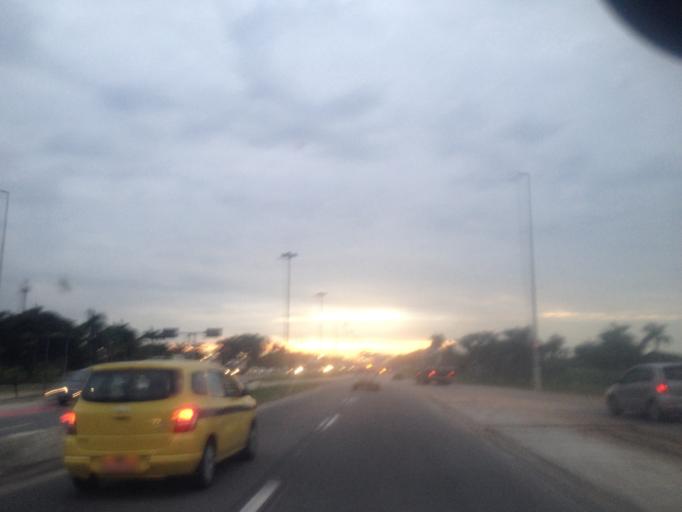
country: BR
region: Rio de Janeiro
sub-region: Rio De Janeiro
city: Rio de Janeiro
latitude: -22.8216
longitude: -43.2325
